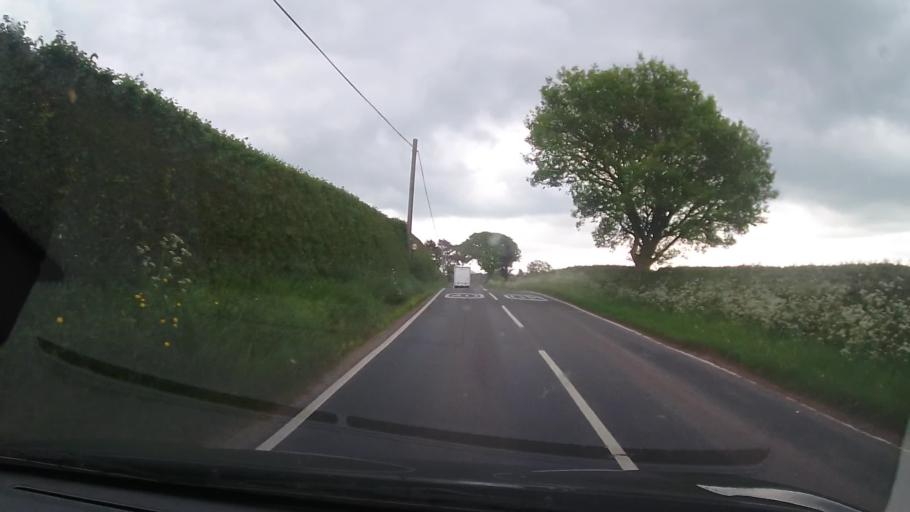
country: GB
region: England
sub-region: Shropshire
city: Ellesmere
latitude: 52.9056
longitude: -2.8214
